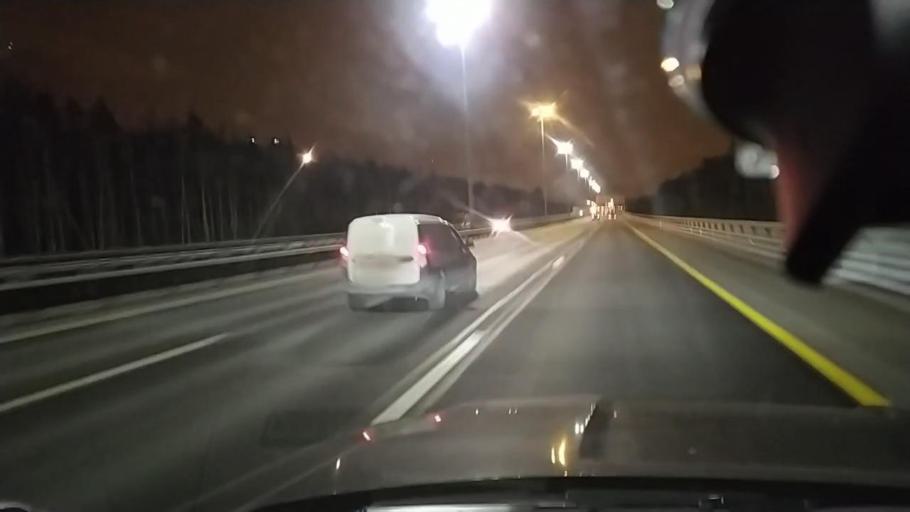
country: RU
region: Leningrad
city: Untolovo
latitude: 60.0326
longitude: 30.1914
